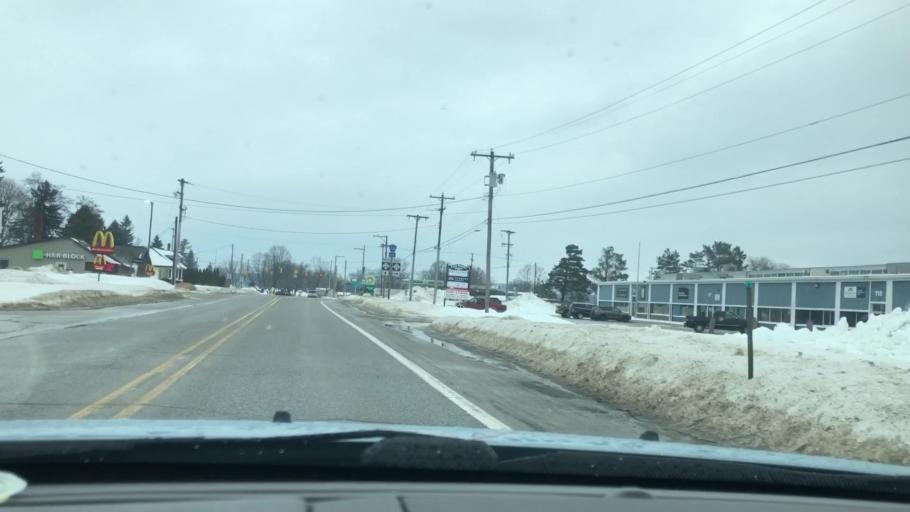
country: US
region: Michigan
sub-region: Charlevoix County
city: East Jordan
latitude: 45.1523
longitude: -85.1399
